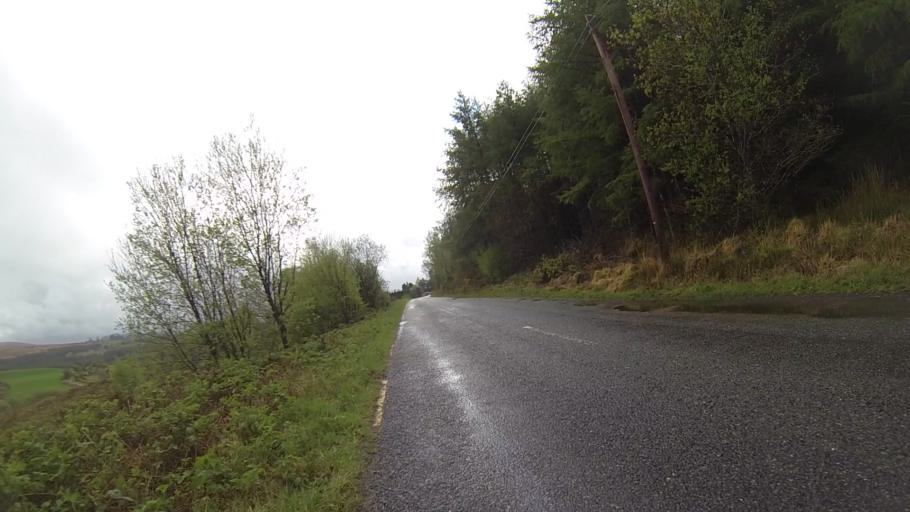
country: IE
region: Munster
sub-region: Ciarrai
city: Kenmare
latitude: 51.9046
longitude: -9.7412
